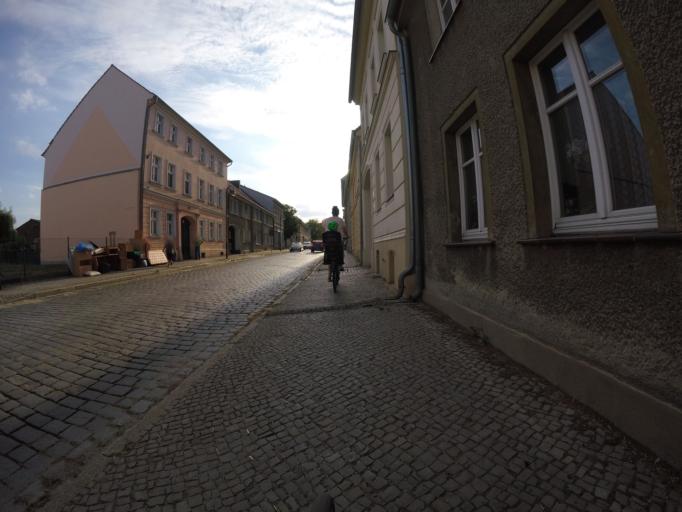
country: DE
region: Brandenburg
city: Altlandsberg
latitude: 52.5649
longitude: 13.7289
